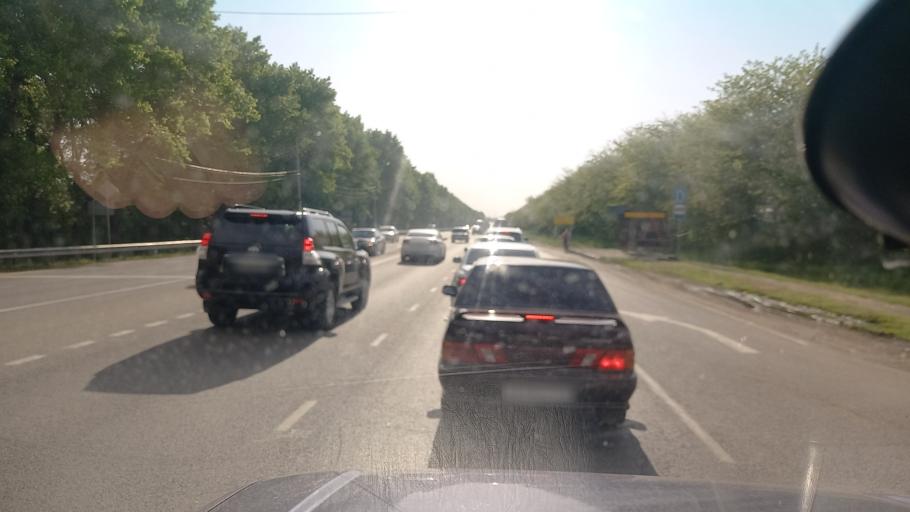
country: RU
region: Adygeya
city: Yablonovskiy
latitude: 45.0566
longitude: 38.8849
